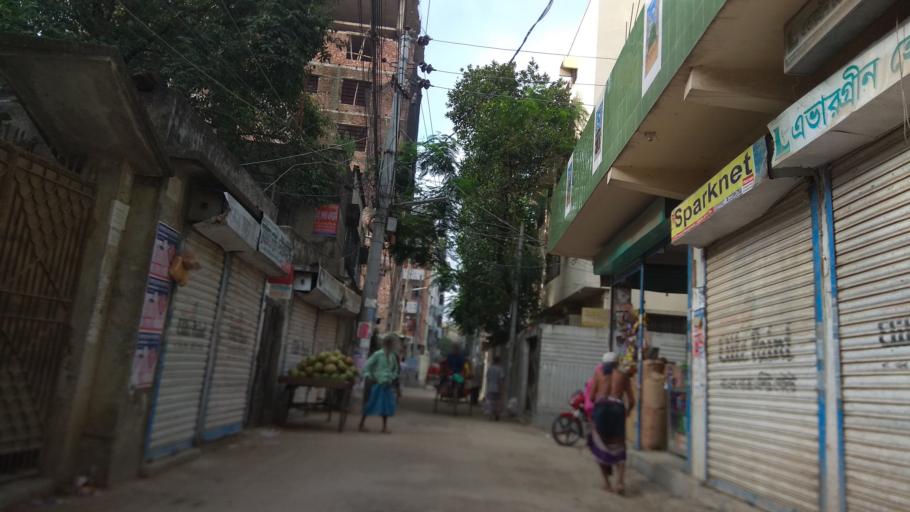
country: BD
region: Dhaka
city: Azimpur
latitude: 23.7943
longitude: 90.3790
